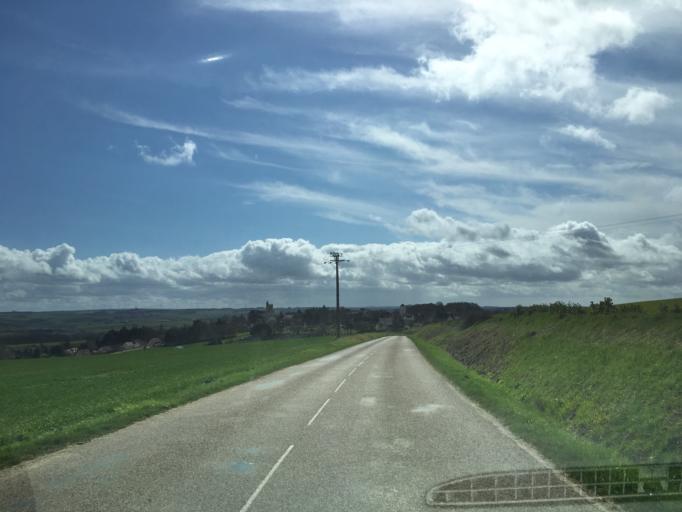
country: FR
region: Bourgogne
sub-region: Departement de l'Yonne
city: Pourrain
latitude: 47.7641
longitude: 3.4115
